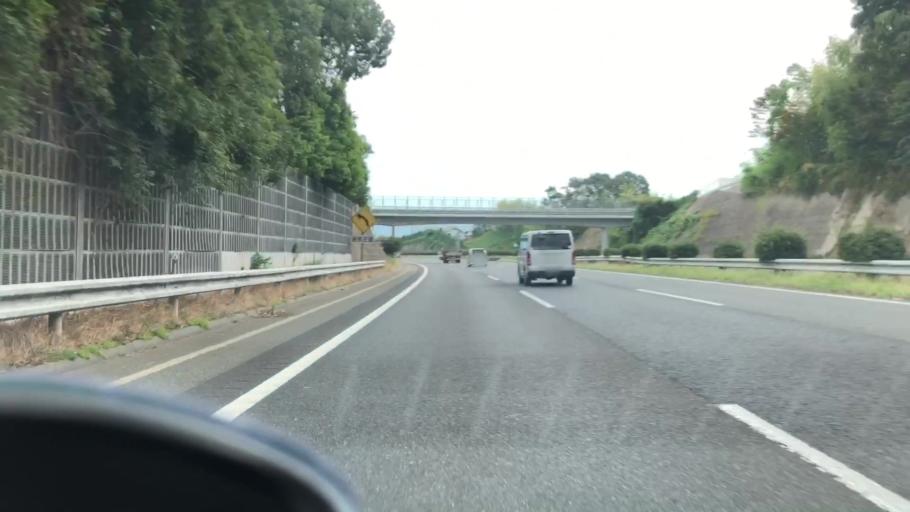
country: JP
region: Hyogo
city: Sandacho
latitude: 34.8721
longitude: 135.1967
